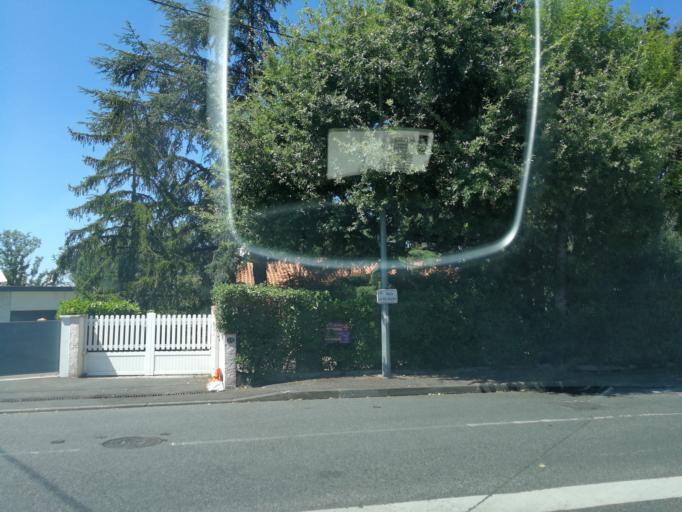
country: FR
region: Midi-Pyrenees
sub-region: Departement de la Haute-Garonne
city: Balma
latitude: 43.6158
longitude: 1.5037
